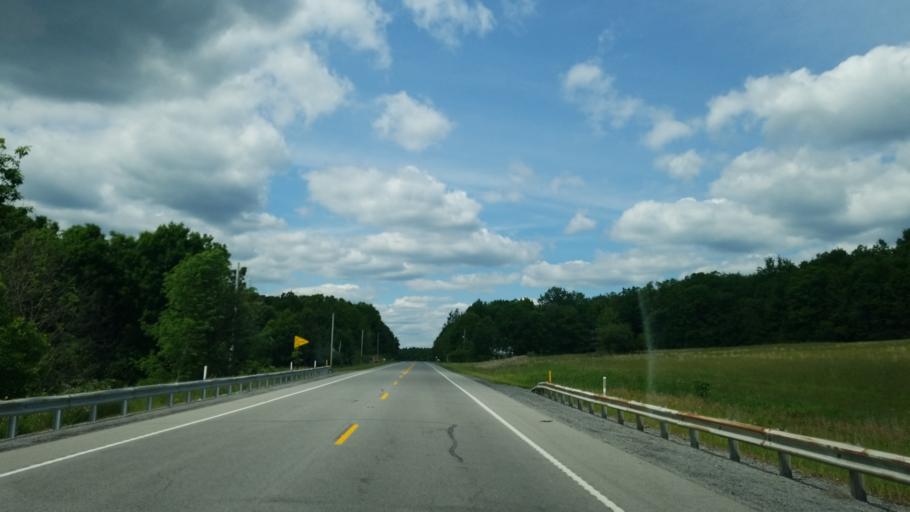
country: US
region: Pennsylvania
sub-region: Clearfield County
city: Osceola Mills
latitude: 40.9021
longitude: -78.3814
